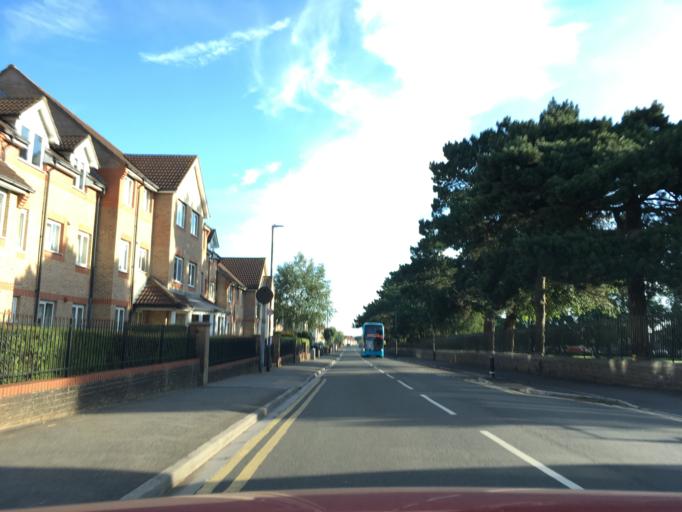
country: GB
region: England
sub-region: South Gloucestershire
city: Mangotsfield
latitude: 51.4819
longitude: -2.5005
